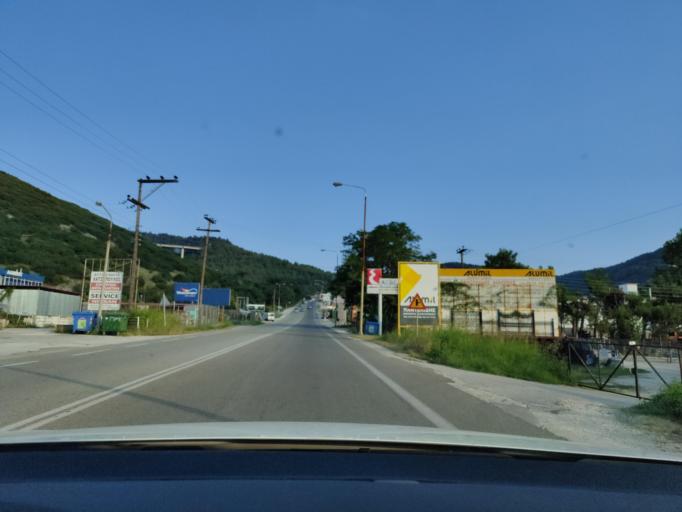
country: GR
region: East Macedonia and Thrace
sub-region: Nomos Kavalas
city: Amygdaleonas
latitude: 40.9554
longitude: 24.3656
